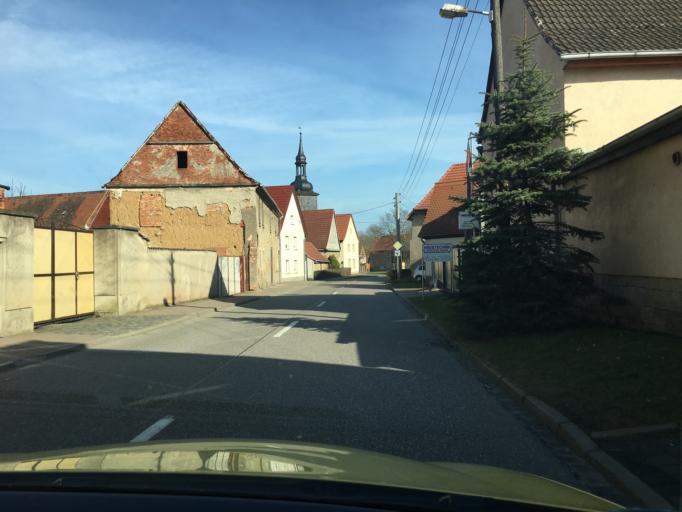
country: DE
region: Thuringia
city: Rastenberg
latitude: 51.2153
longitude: 11.4794
